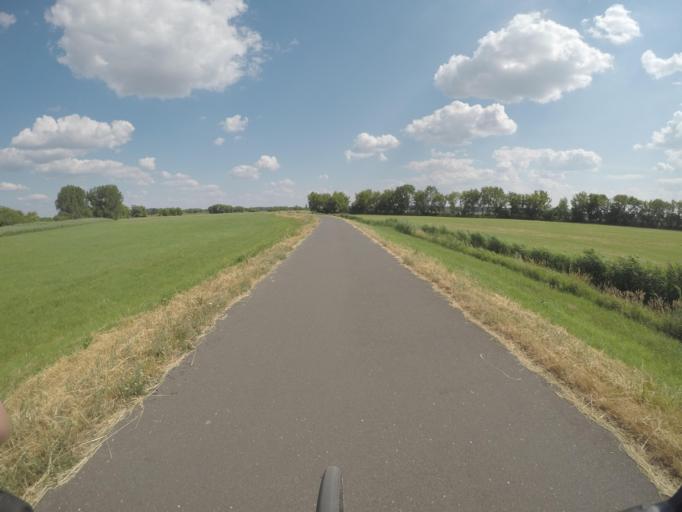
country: DE
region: Brandenburg
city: Ketzin
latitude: 52.4557
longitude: 12.8686
